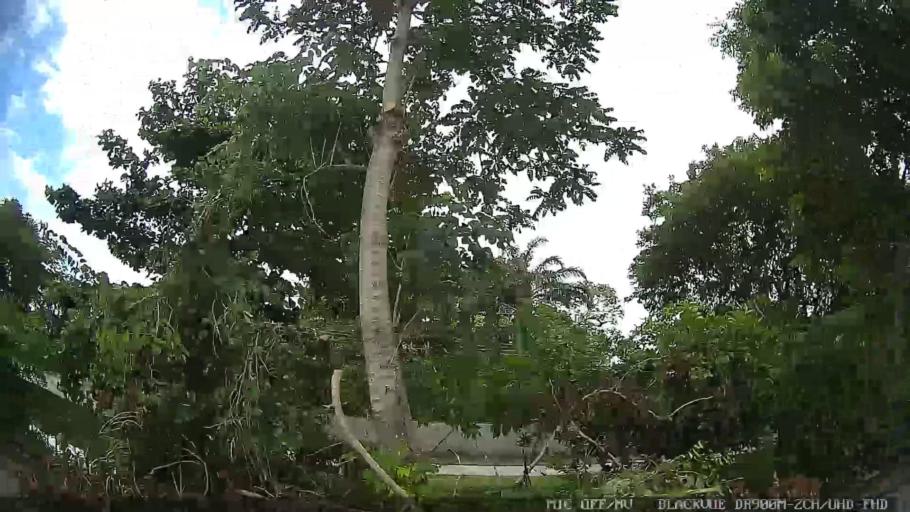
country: BR
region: Sao Paulo
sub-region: Caraguatatuba
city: Caraguatatuba
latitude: -23.6414
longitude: -45.4369
